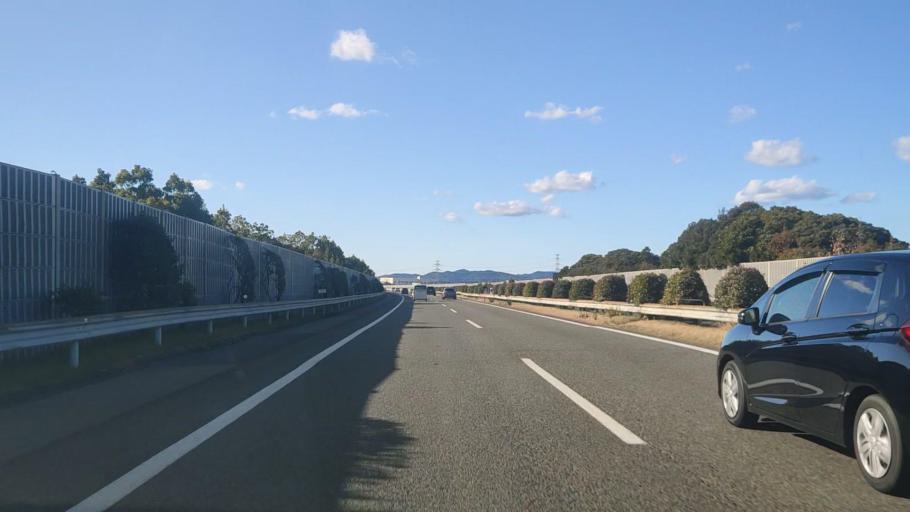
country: JP
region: Fukuoka
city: Nogata
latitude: 33.7824
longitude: 130.7276
